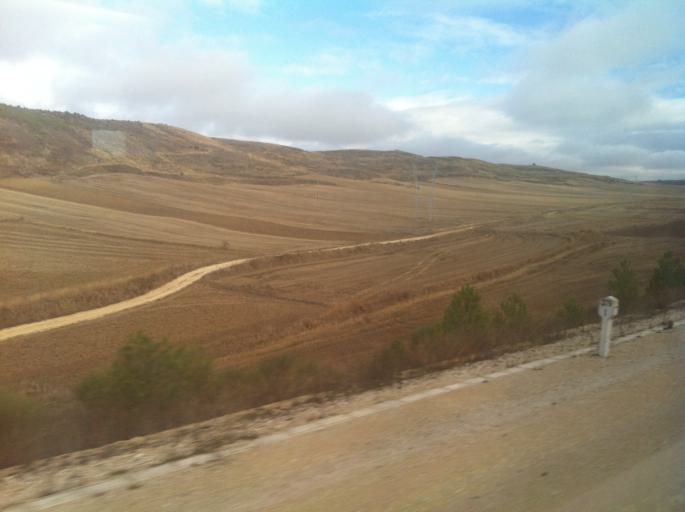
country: ES
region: Castille and Leon
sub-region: Provincia de Burgos
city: Rubena
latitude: 42.3774
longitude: -3.5994
